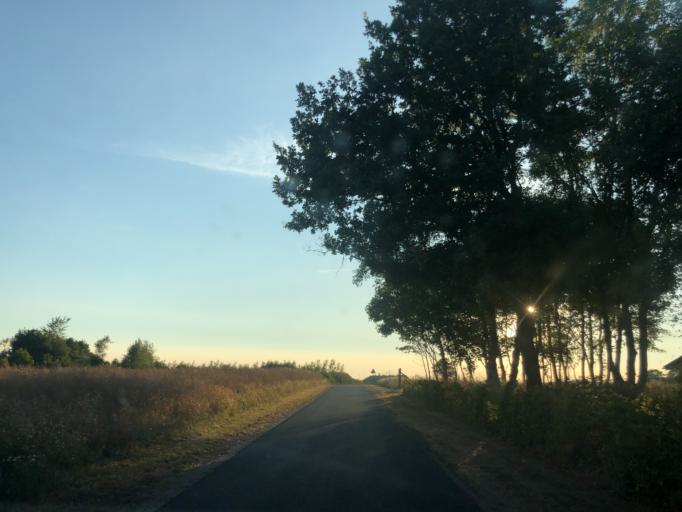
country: DK
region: Central Jutland
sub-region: Holstebro Kommune
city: Holstebro
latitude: 56.3712
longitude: 8.6751
